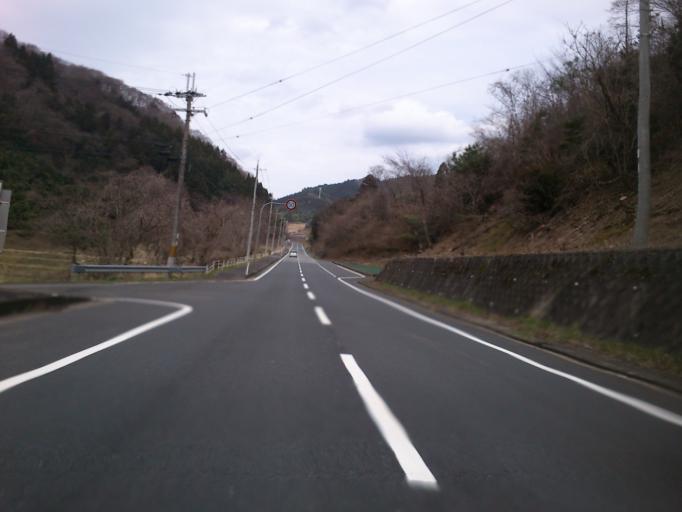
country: JP
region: Kyoto
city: Fukuchiyama
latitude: 35.3890
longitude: 135.0953
